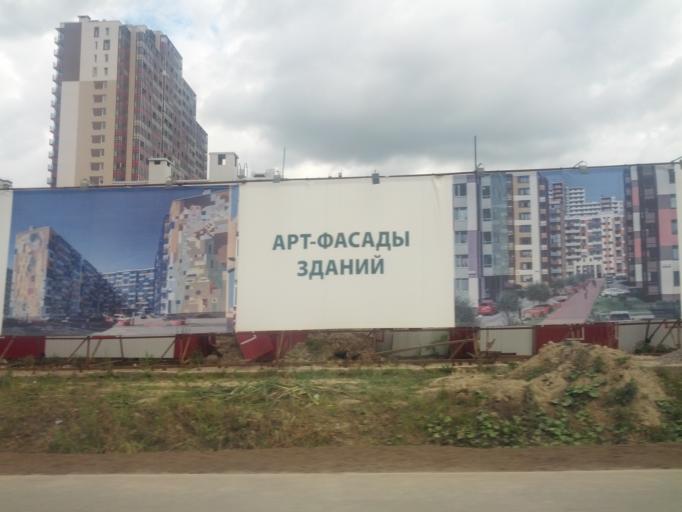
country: RU
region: Leningrad
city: Rybatskoye
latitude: 59.9002
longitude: 30.5053
